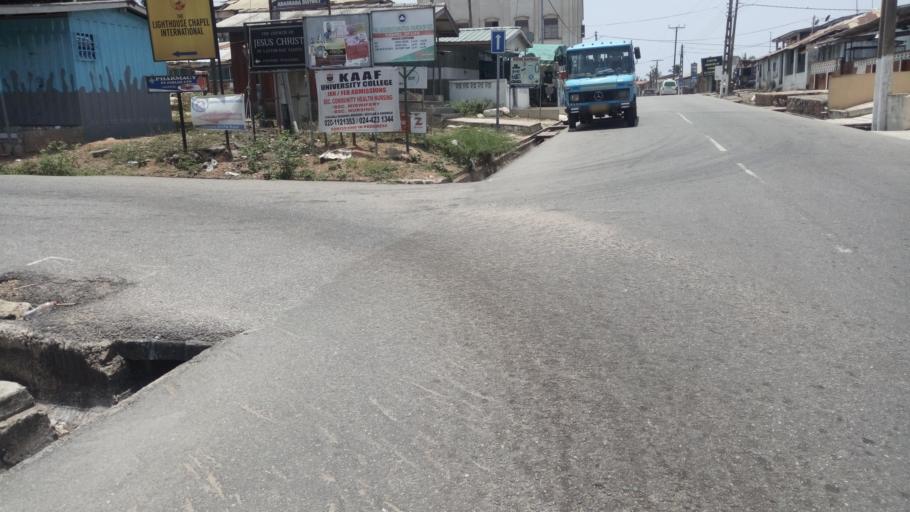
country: GH
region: Central
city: Winneba
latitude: 5.3446
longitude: -0.6279
